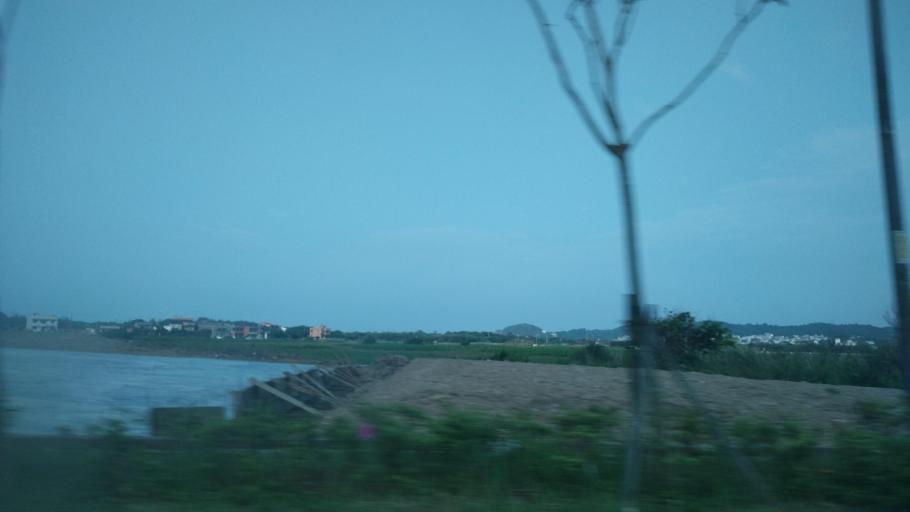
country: TW
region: Taiwan
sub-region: Keelung
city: Keelung
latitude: 25.2330
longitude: 121.6297
